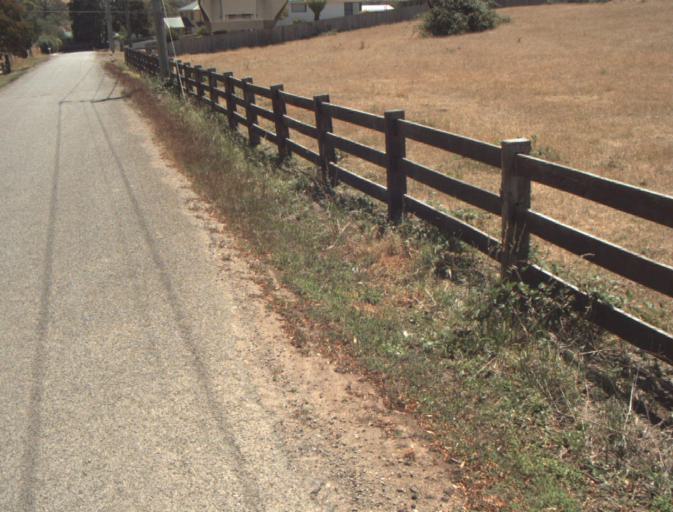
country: AU
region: Tasmania
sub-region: Launceston
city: Mayfield
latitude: -41.3711
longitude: 147.1418
